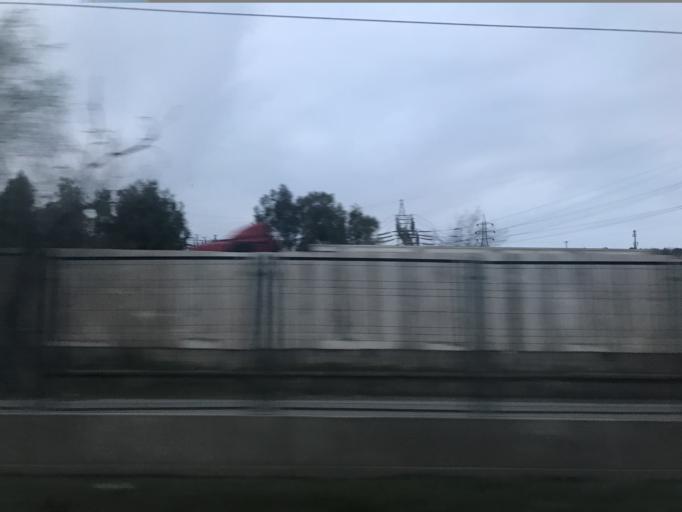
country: TR
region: Kocaeli
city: Darica
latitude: 40.8049
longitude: 29.3714
